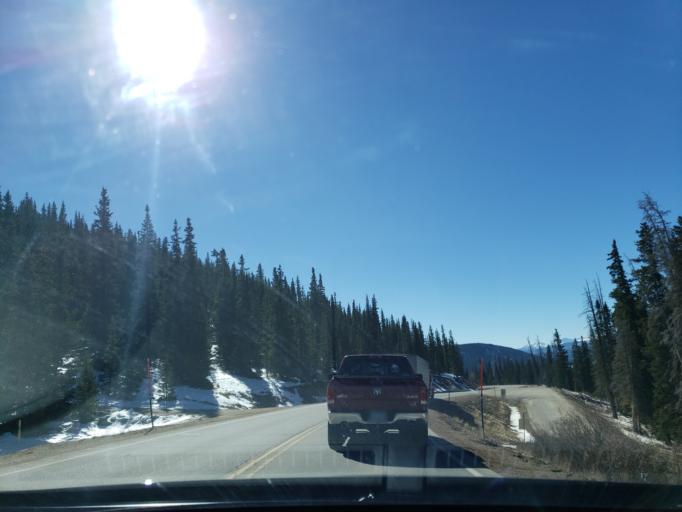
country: US
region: Colorado
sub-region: Summit County
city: Breckenridge
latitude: 39.3502
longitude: -106.0548
